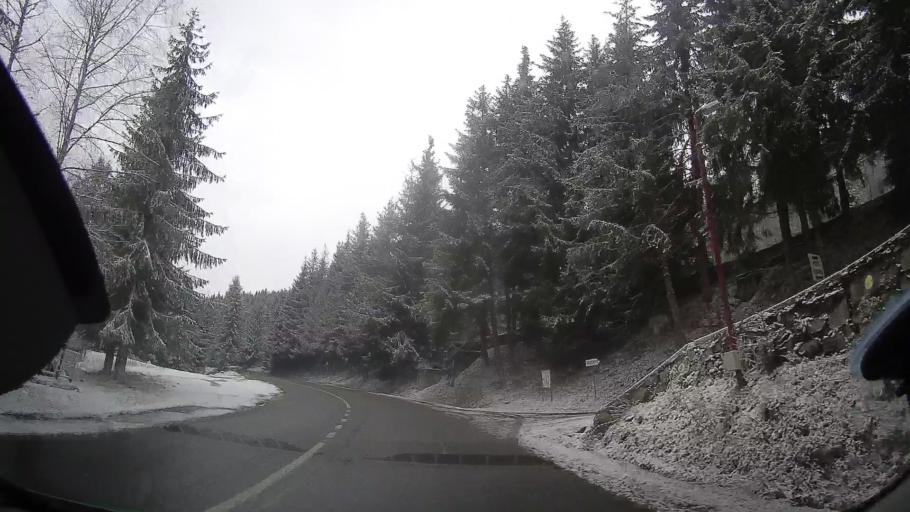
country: RO
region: Cluj
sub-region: Comuna Belis
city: Belis
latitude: 46.6688
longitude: 23.0554
